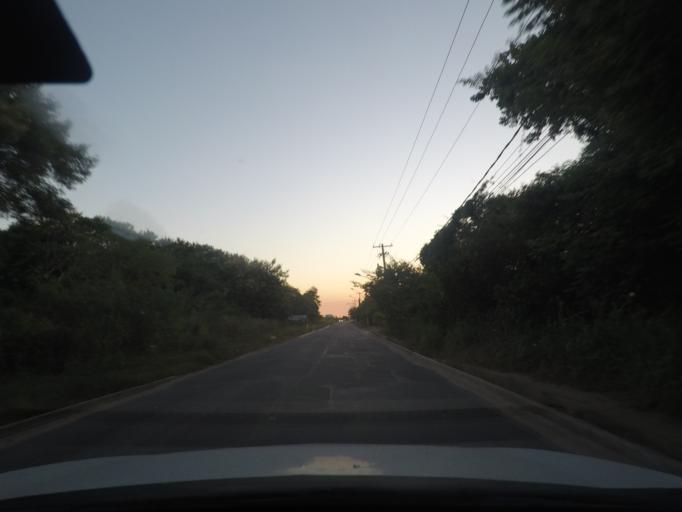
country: BR
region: Rio de Janeiro
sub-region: Niteroi
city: Niteroi
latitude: -22.9526
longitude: -42.9741
